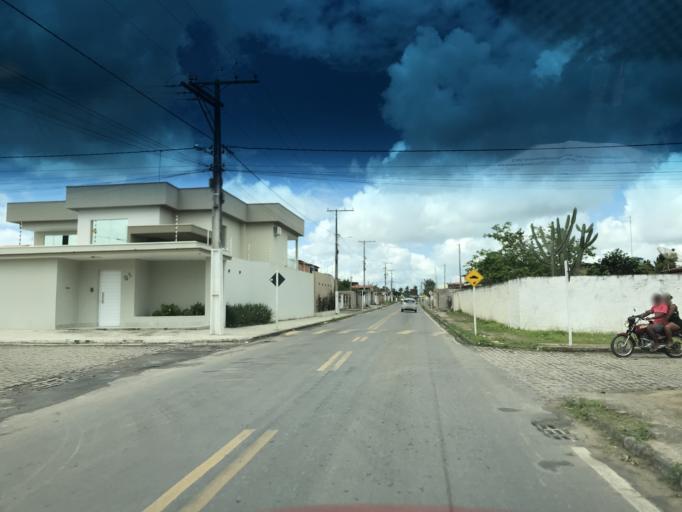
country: BR
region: Bahia
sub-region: Conceicao Do Almeida
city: Conceicao do Almeida
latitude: -12.7351
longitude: -39.1880
